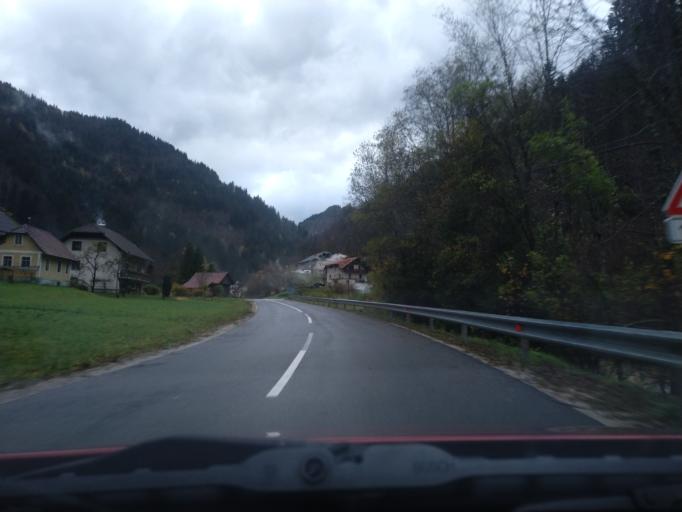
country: SI
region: Solcava
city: Solcava
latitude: 46.4199
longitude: 14.6767
